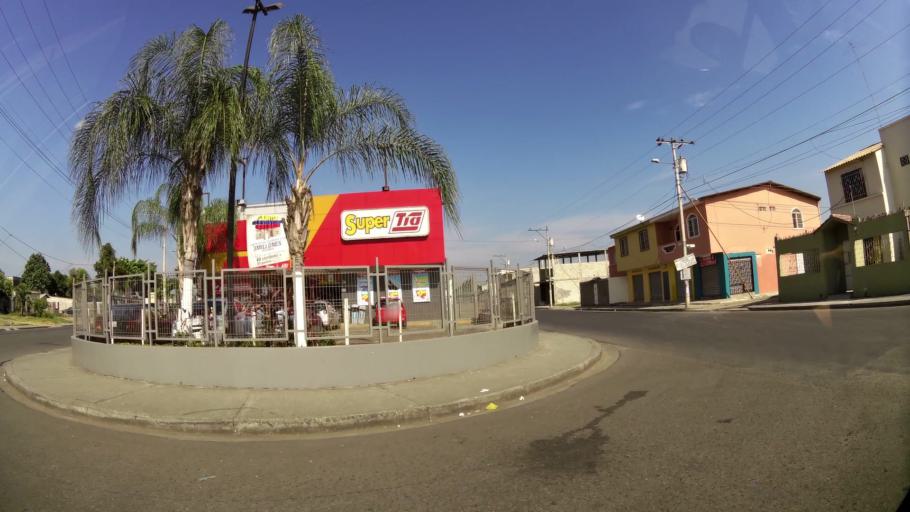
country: EC
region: Guayas
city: Eloy Alfaro
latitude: -2.0982
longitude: -79.9178
